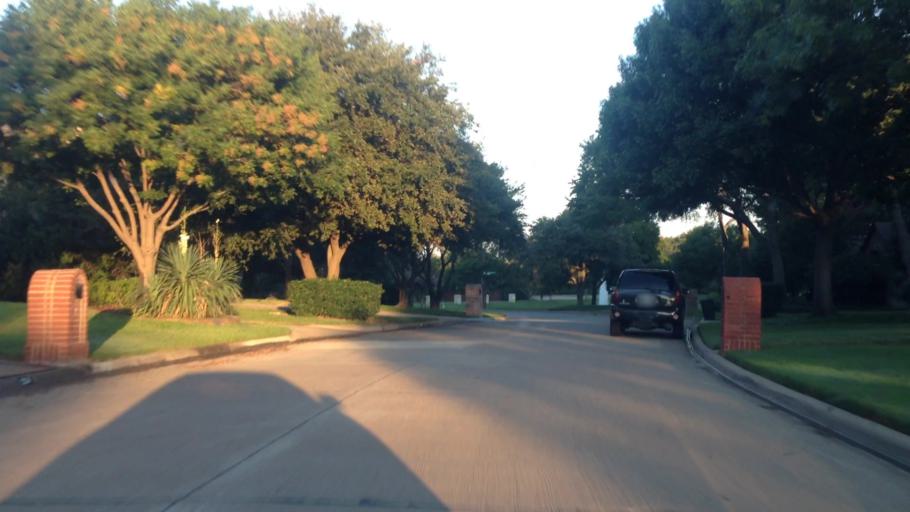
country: US
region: Texas
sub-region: Tarrant County
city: Southlake
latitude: 32.9395
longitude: -97.1619
